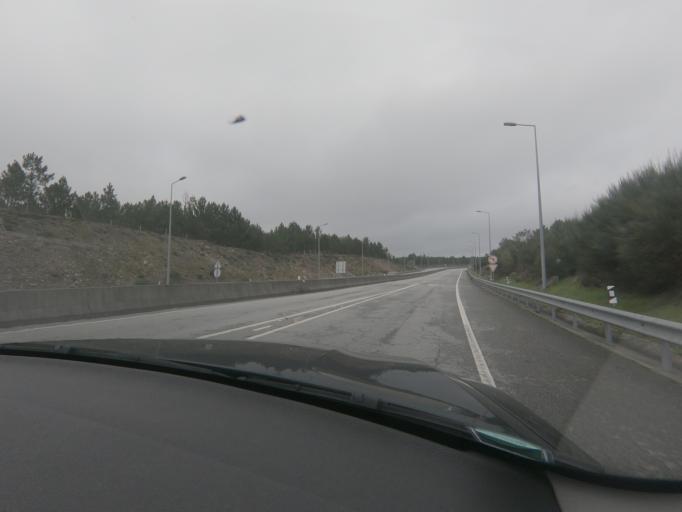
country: PT
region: Viseu
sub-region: Viseu
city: Abraveses
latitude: 40.6736
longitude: -7.9713
